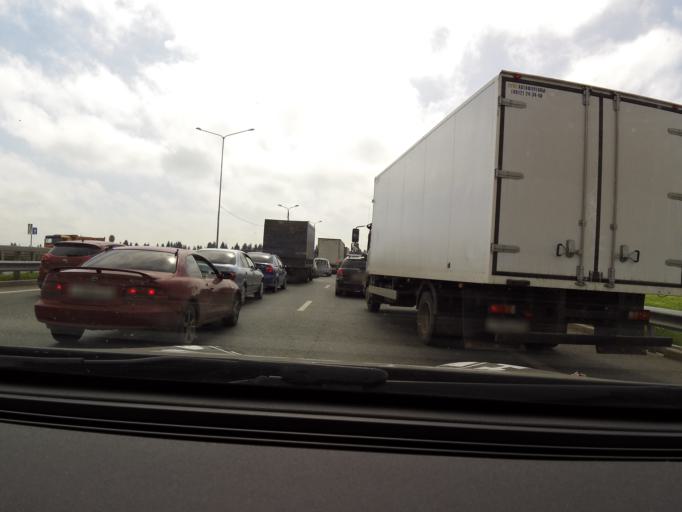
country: RU
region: Perm
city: Lobanovo
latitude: 57.8420
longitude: 56.2962
